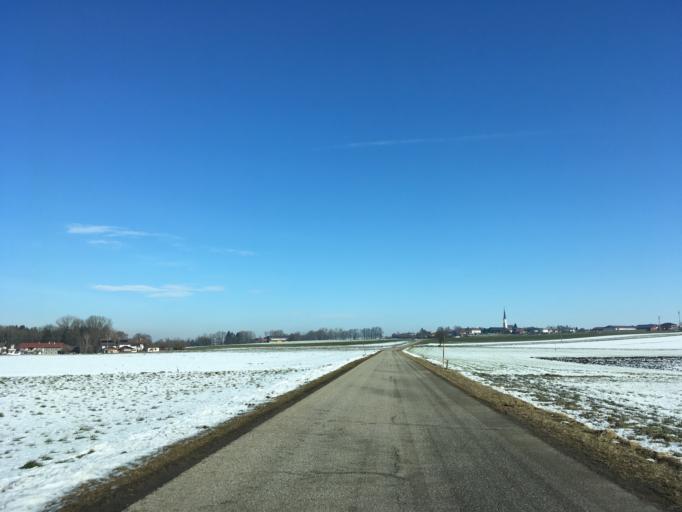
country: DE
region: Bavaria
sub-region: Upper Bavaria
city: Griesstatt
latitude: 47.9840
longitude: 12.1654
